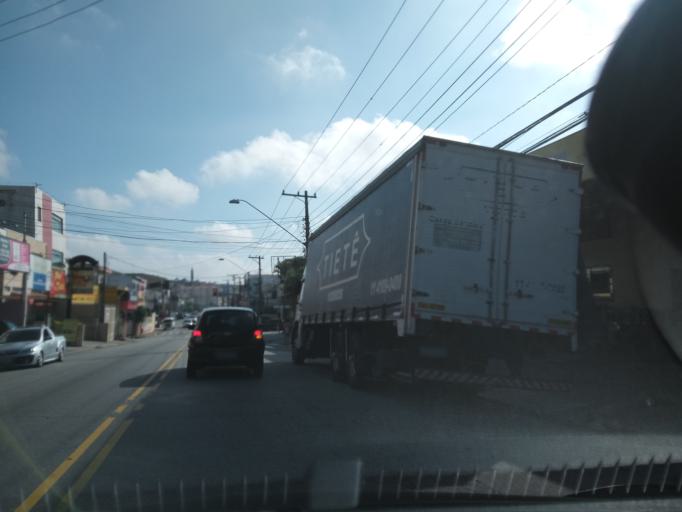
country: BR
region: Sao Paulo
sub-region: Sao Bernardo Do Campo
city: Sao Bernardo do Campo
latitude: -23.7284
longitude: -46.5656
